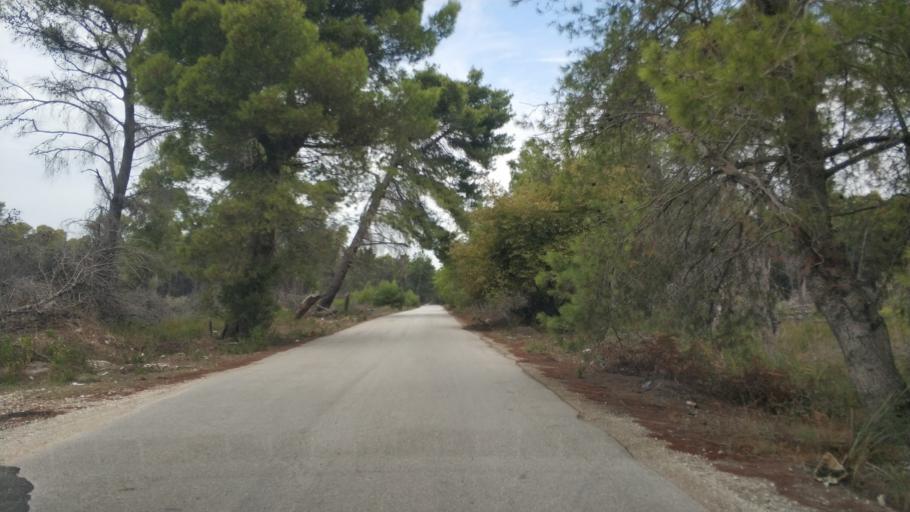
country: AL
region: Vlore
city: Vlore
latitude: 40.4801
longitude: 19.4501
